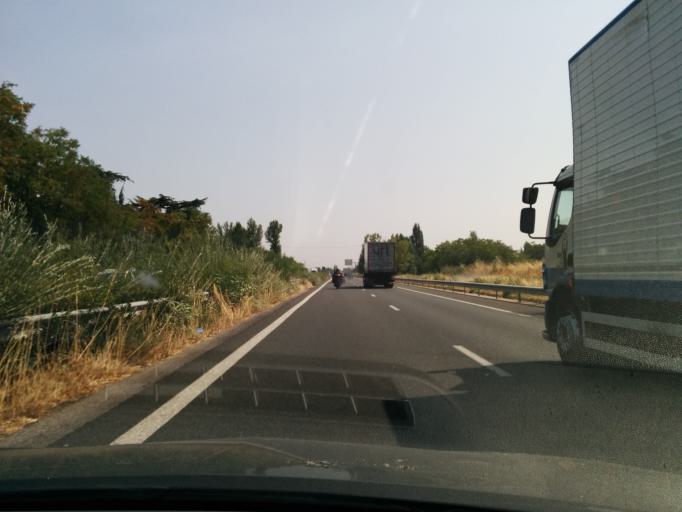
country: FR
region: Midi-Pyrenees
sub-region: Departement du Tarn
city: Marssac-sur-Tarn
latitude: 43.9102
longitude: 2.0476
